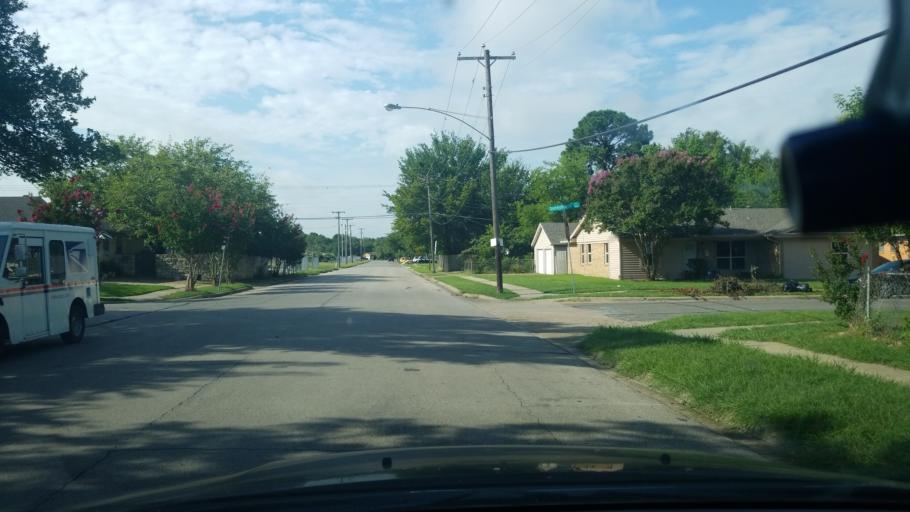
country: US
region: Texas
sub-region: Dallas County
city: Balch Springs
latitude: 32.7480
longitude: -96.6698
